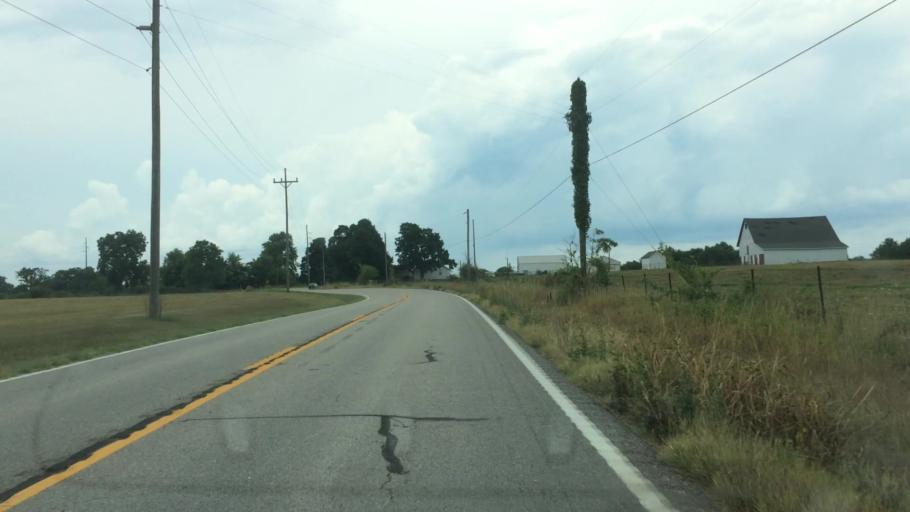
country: US
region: Missouri
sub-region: Greene County
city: Strafford
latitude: 37.2513
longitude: -93.1353
